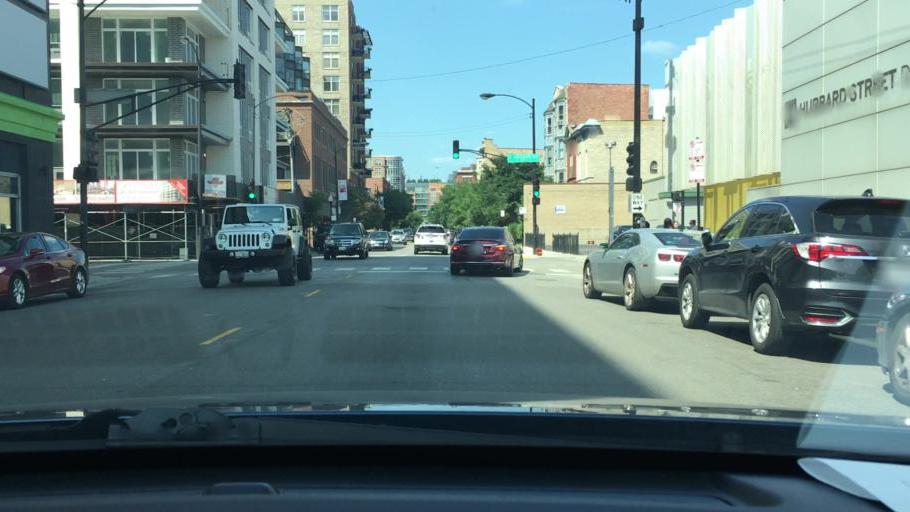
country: US
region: Illinois
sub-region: Cook County
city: Chicago
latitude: 41.8775
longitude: -87.6570
